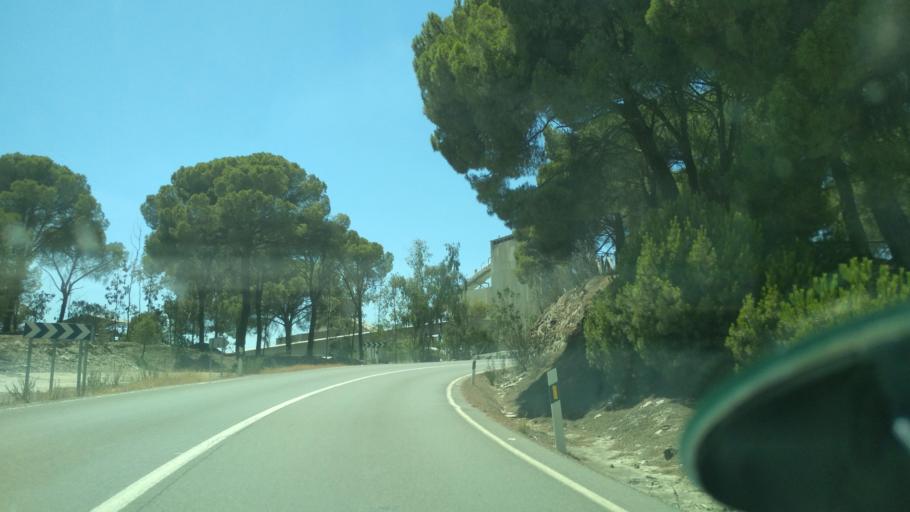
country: ES
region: Andalusia
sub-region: Provincia de Huelva
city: Nerva
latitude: 37.7130
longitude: -6.5811
